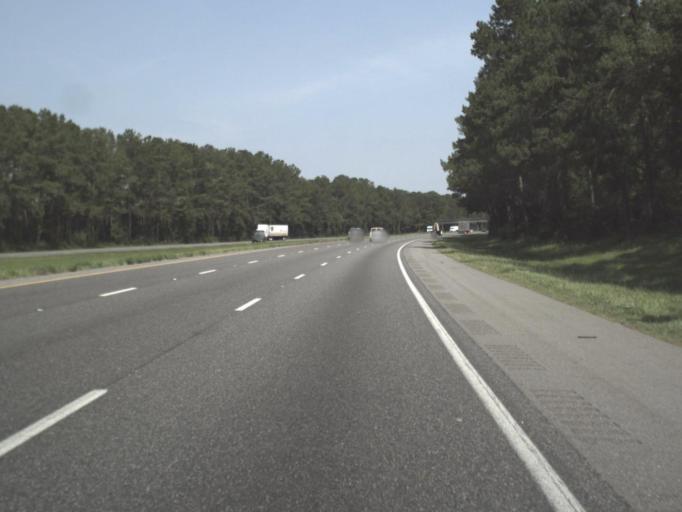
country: US
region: Florida
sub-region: Suwannee County
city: Wellborn
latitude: 30.3690
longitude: -82.8582
